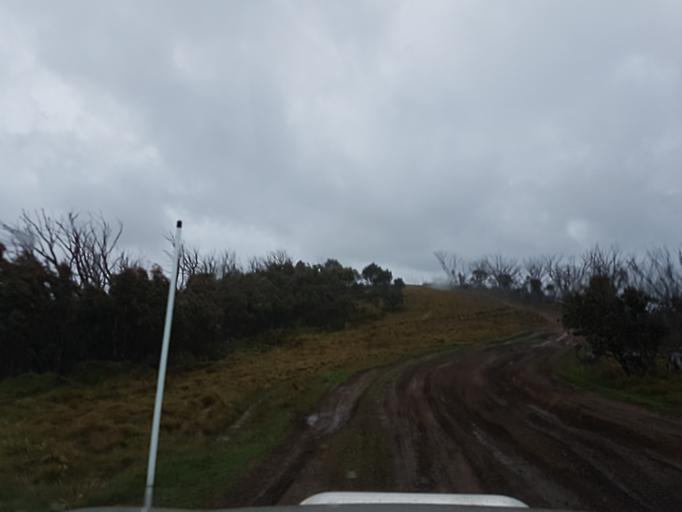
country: AU
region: Victoria
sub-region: Alpine
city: Mount Beauty
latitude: -37.0860
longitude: 147.1084
